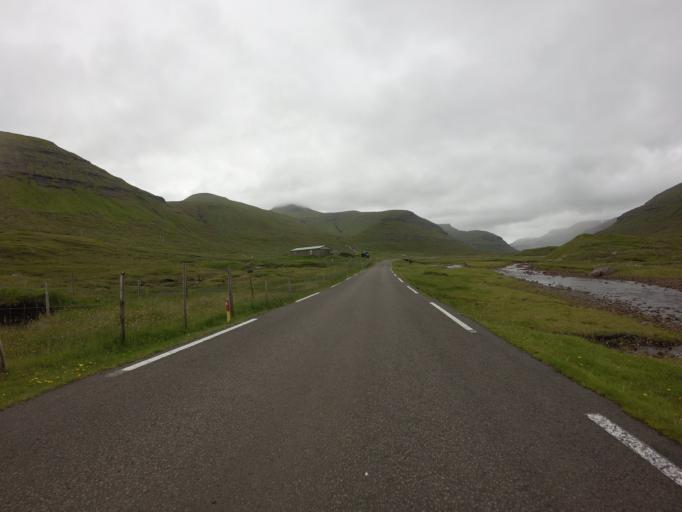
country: FO
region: Streymoy
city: Vestmanna
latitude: 62.2049
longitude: -7.0971
